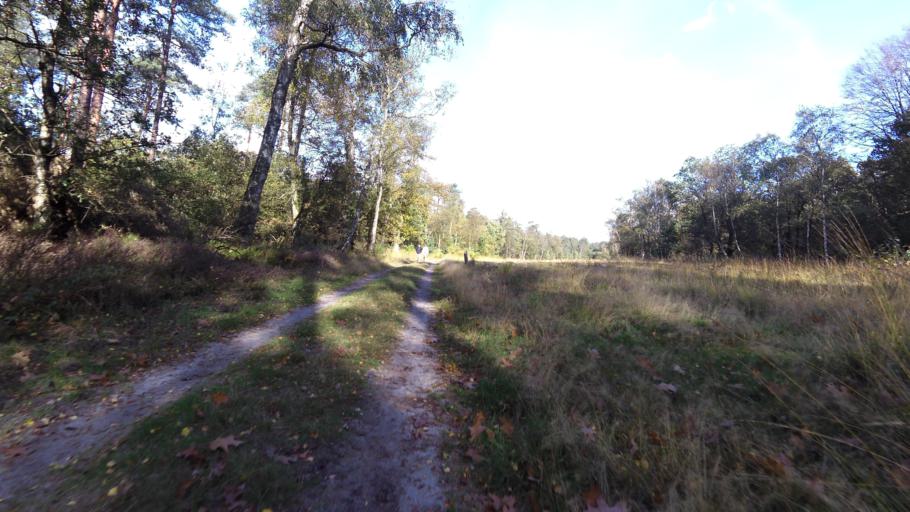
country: NL
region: Gelderland
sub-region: Gemeente Epe
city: Emst
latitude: 52.3318
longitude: 5.8760
